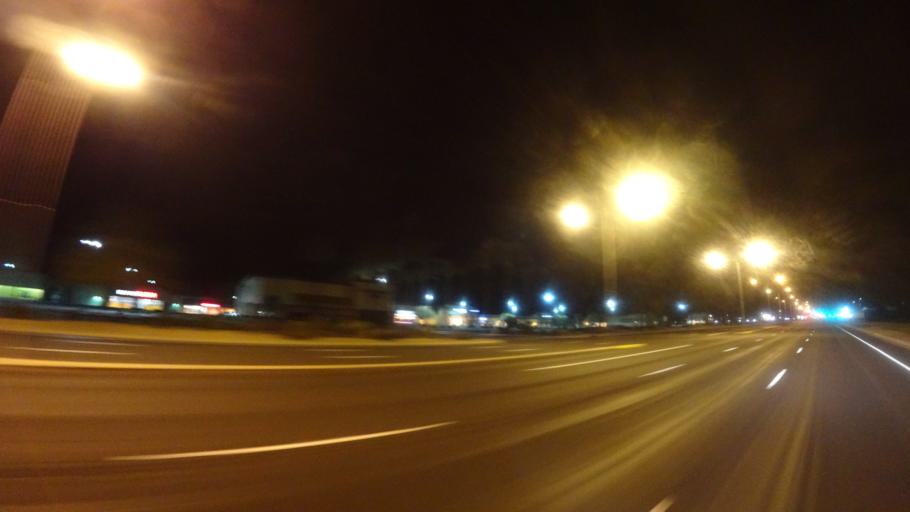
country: US
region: Arizona
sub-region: Maricopa County
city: Gilbert
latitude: 33.4155
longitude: -111.7000
